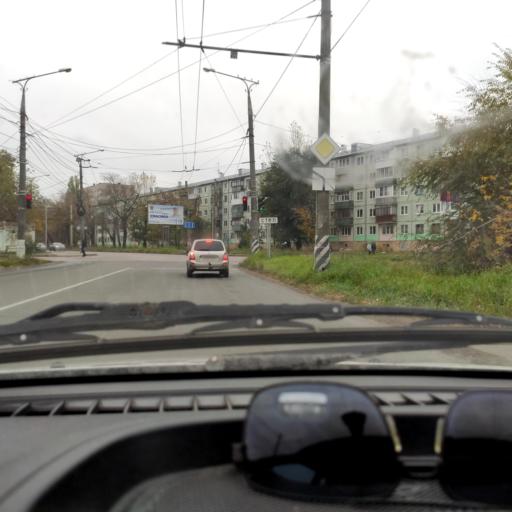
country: RU
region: Samara
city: Tol'yatti
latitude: 53.5149
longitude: 49.4294
